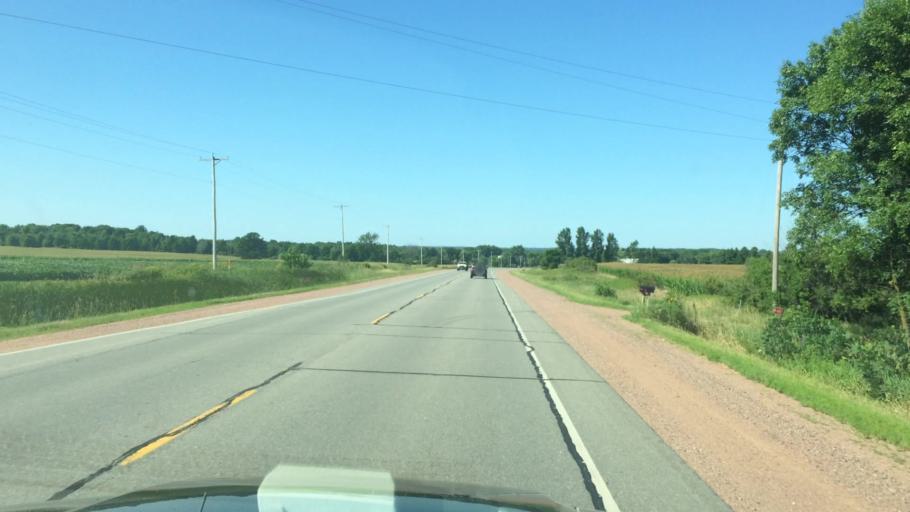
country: US
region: Wisconsin
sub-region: Marathon County
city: Stratford
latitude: 44.7285
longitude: -90.0893
